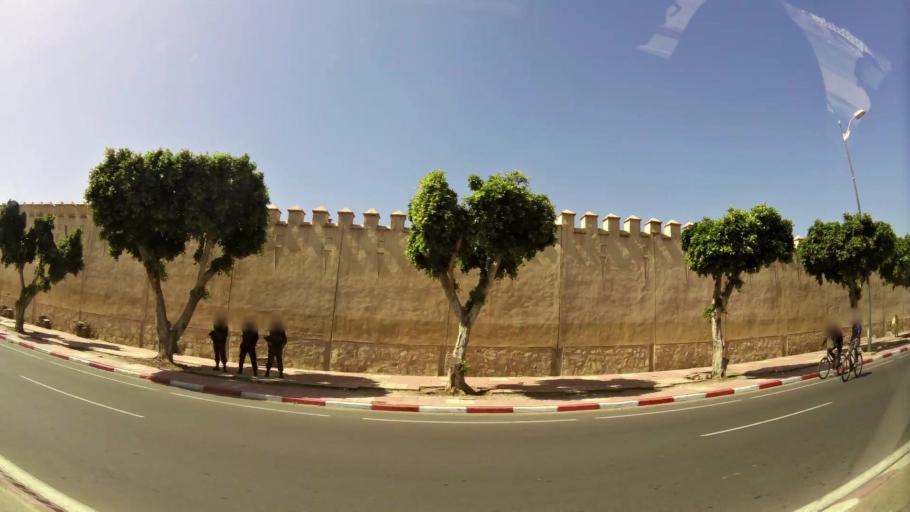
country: MA
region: Souss-Massa-Draa
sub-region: Agadir-Ida-ou-Tnan
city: Agadir
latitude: 30.4110
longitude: -9.5806
